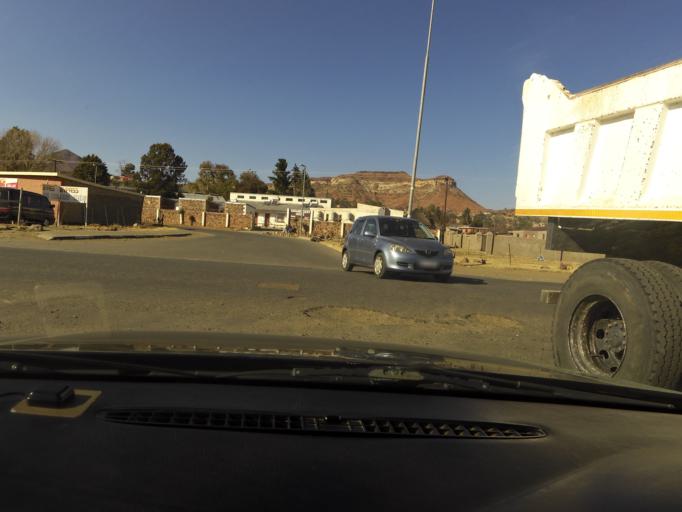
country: LS
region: Mohale's Hoek District
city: Mohale's Hoek
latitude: -30.1503
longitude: 27.4595
